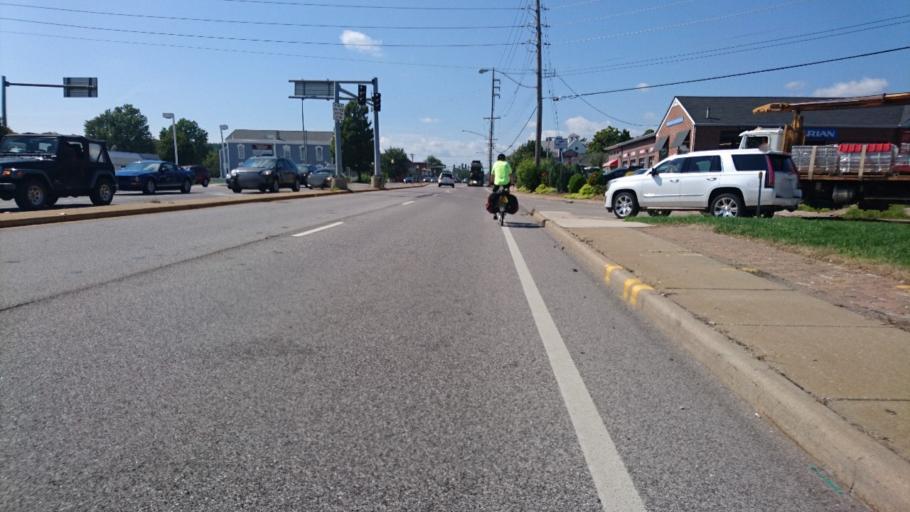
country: US
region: Missouri
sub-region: Saint Louis County
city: Manchester
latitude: 38.5930
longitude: -90.5091
